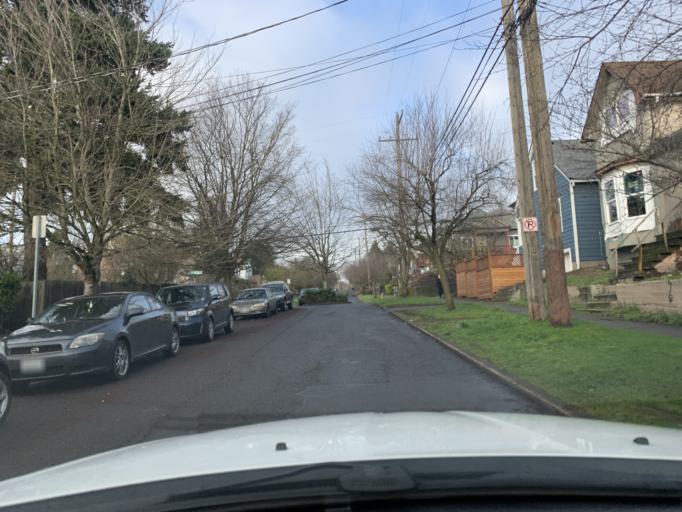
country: US
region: Washington
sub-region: King County
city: Seattle
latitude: 47.6039
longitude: -122.3128
